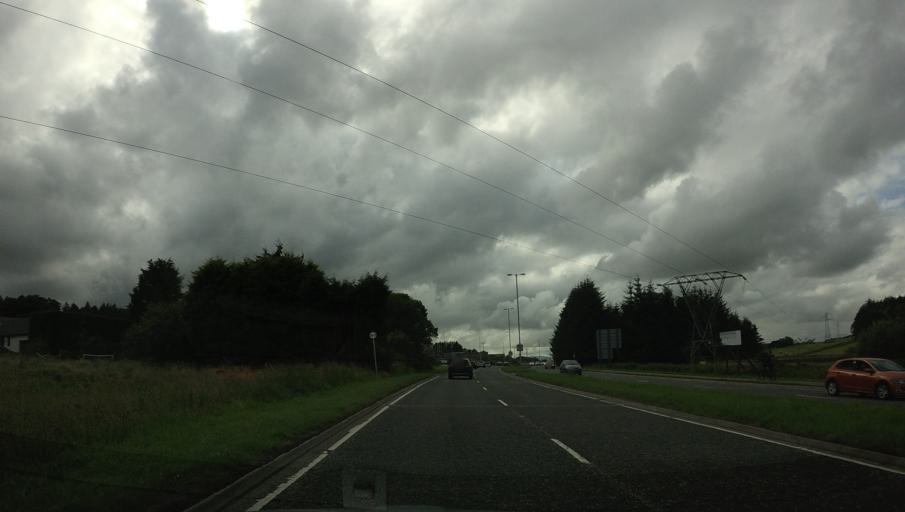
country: GB
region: Scotland
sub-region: Aberdeenshire
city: Westhill
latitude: 57.1462
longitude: -2.2321
